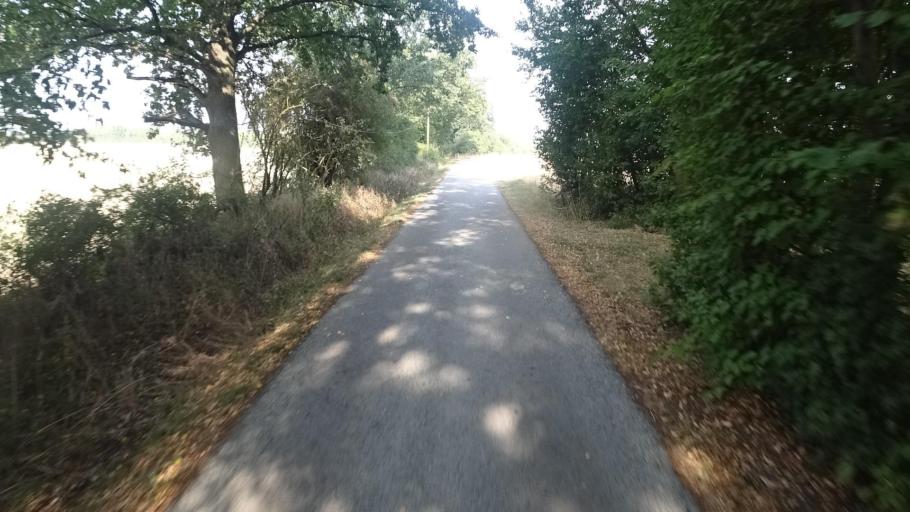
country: DE
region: Rheinland-Pfalz
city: Simmern
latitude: 49.9719
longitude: 7.5200
